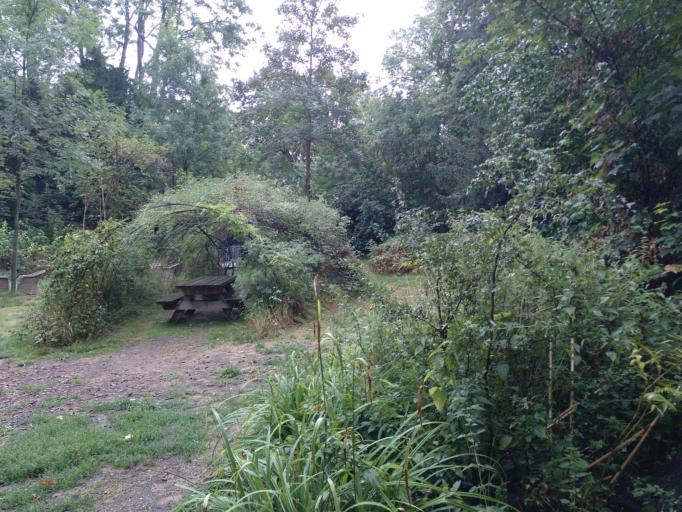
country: FR
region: Ile-de-France
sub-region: Departement des Hauts-de-Seine
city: Suresnes
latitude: 48.8658
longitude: 2.2378
